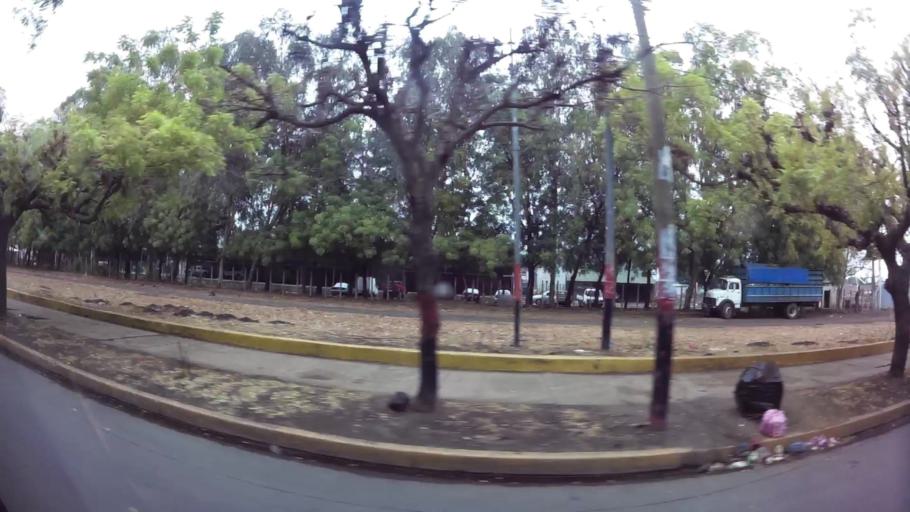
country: NI
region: Leon
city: Leon
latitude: 12.4474
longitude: -86.8718
